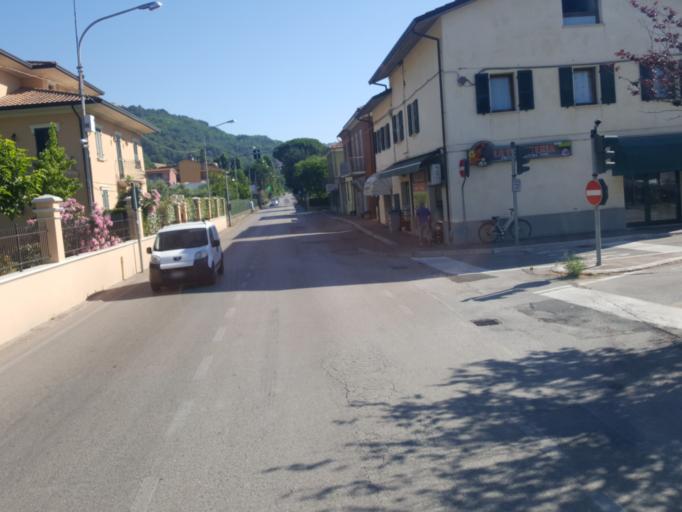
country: IT
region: The Marches
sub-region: Provincia di Pesaro e Urbino
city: Borgo Massano
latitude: 43.8300
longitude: 12.6829
